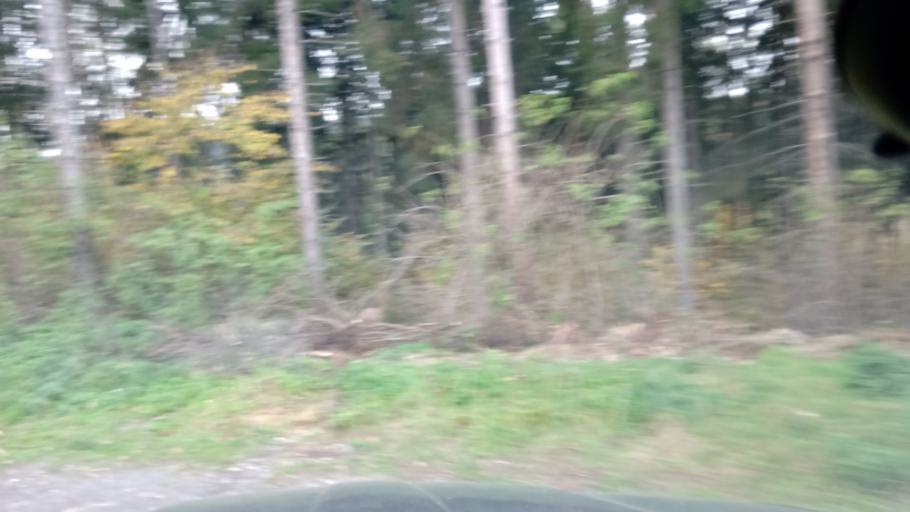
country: AT
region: Styria
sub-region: Politischer Bezirk Leoben
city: Leoben
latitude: 47.3924
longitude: 15.1080
